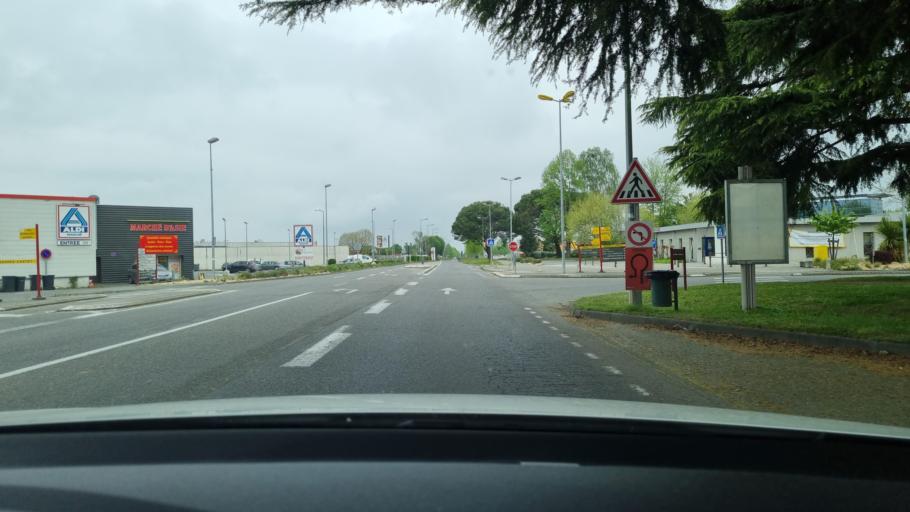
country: FR
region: Aquitaine
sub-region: Departement des Pyrenees-Atlantiques
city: Montardon
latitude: 43.3585
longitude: -0.3813
